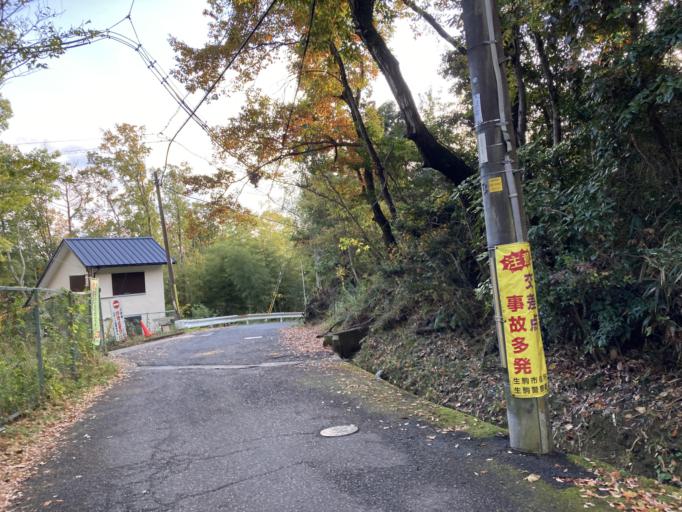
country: JP
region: Nara
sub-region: Ikoma-shi
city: Ikoma
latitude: 34.6750
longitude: 135.6908
